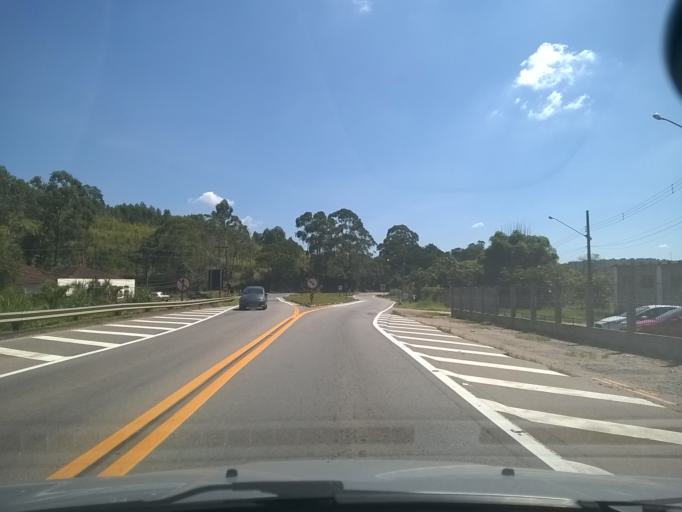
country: BR
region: Sao Paulo
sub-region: Varzea Paulista
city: Varzea Paulista
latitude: -23.2577
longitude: -46.8357
